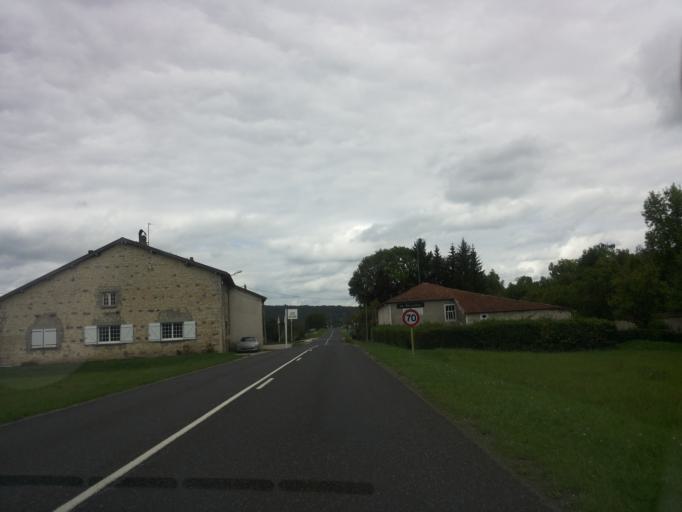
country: FR
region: Lorraine
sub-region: Departement de la Meuse
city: Ligny-en-Barrois
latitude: 48.6480
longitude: 5.3505
